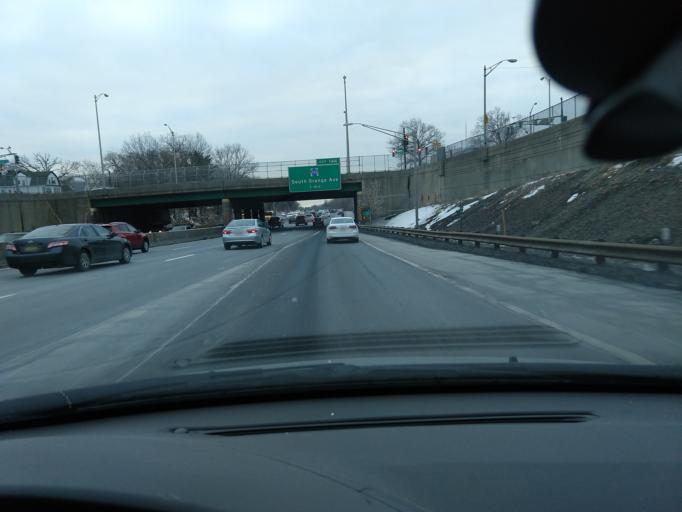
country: US
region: New Jersey
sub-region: Essex County
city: East Orange
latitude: 40.7537
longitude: -74.2110
